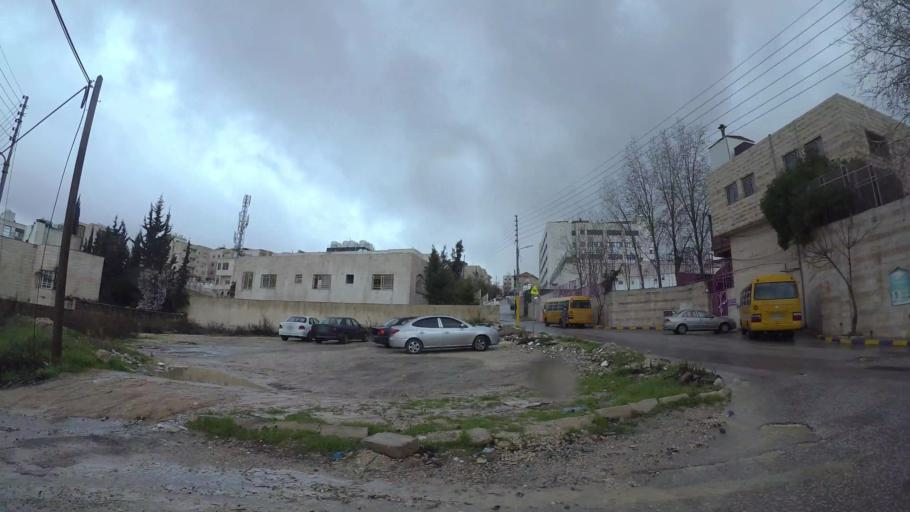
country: JO
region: Amman
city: Al Jubayhah
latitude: 32.0347
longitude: 35.8900
